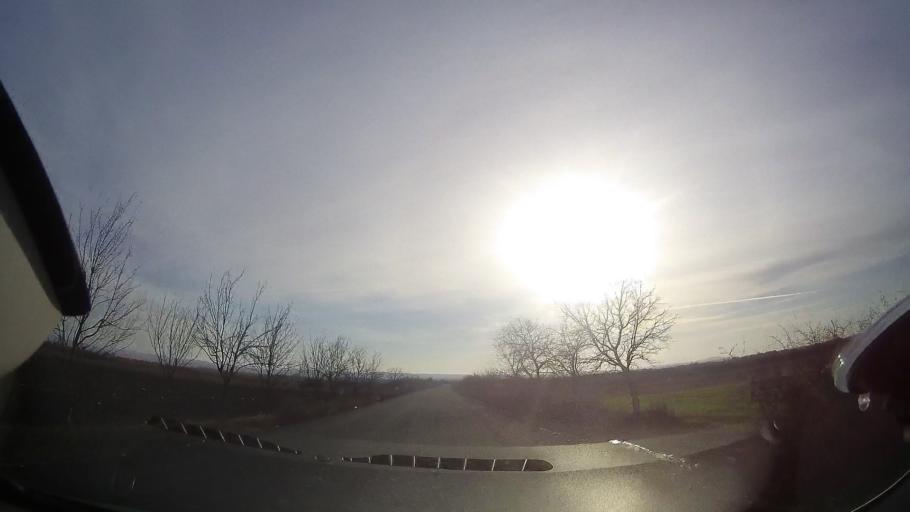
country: RO
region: Bihor
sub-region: Comuna Tileagd
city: Tileagd
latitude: 47.0911
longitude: 22.1778
